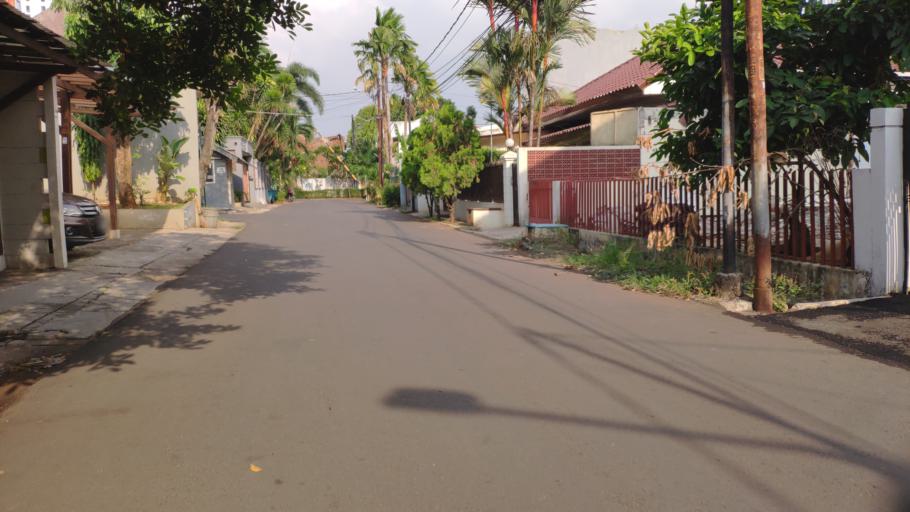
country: ID
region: West Java
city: Pamulang
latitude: -6.2961
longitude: 106.8025
